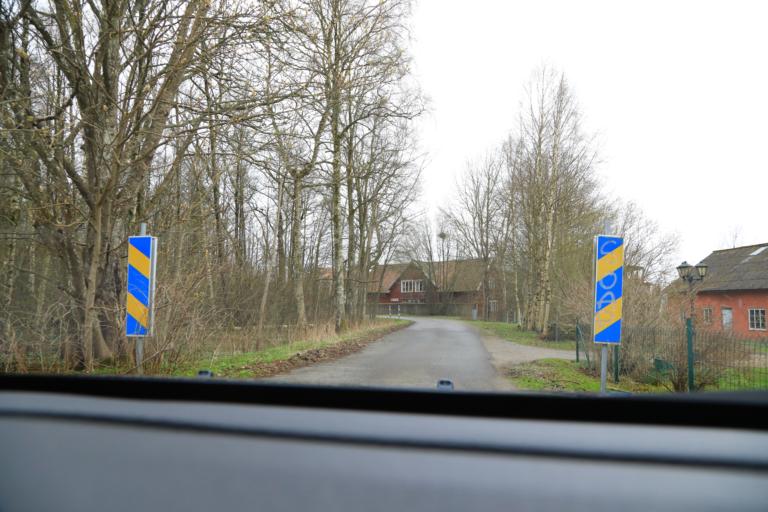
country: SE
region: Halland
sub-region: Kungsbacka Kommun
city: Frillesas
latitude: 57.3106
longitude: 12.1816
